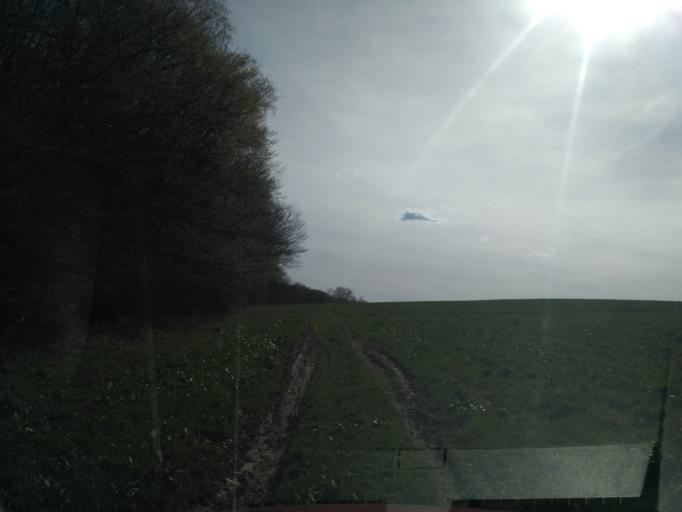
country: SK
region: Presovsky
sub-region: Okres Presov
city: Presov
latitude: 48.9176
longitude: 21.2189
